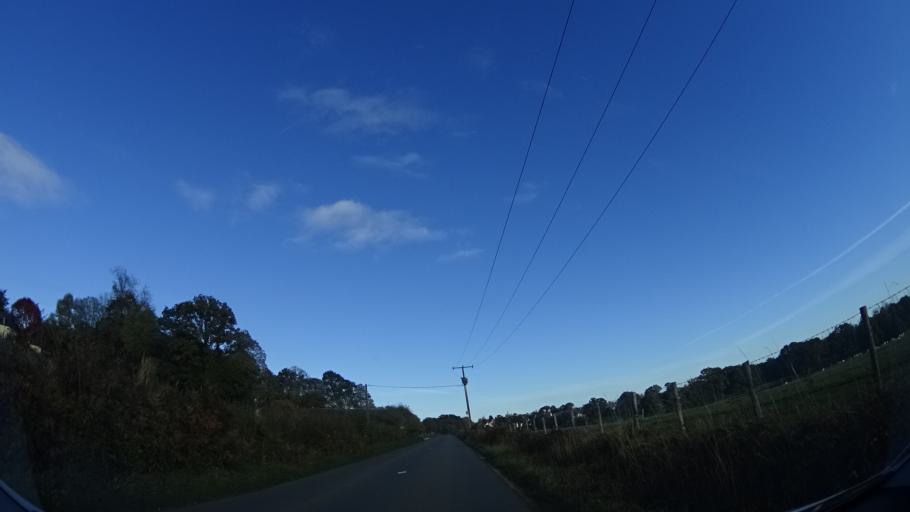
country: FR
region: Brittany
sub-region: Departement d'Ille-et-Vilaine
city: Geveze
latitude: 48.2103
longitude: -1.7912
